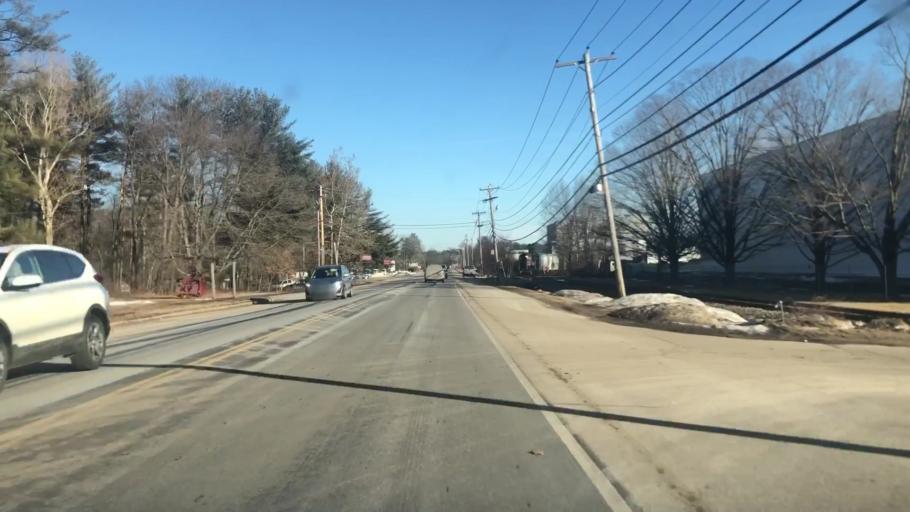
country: US
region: New Hampshire
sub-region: Hillsborough County
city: Wilton
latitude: 42.8419
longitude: -71.6994
